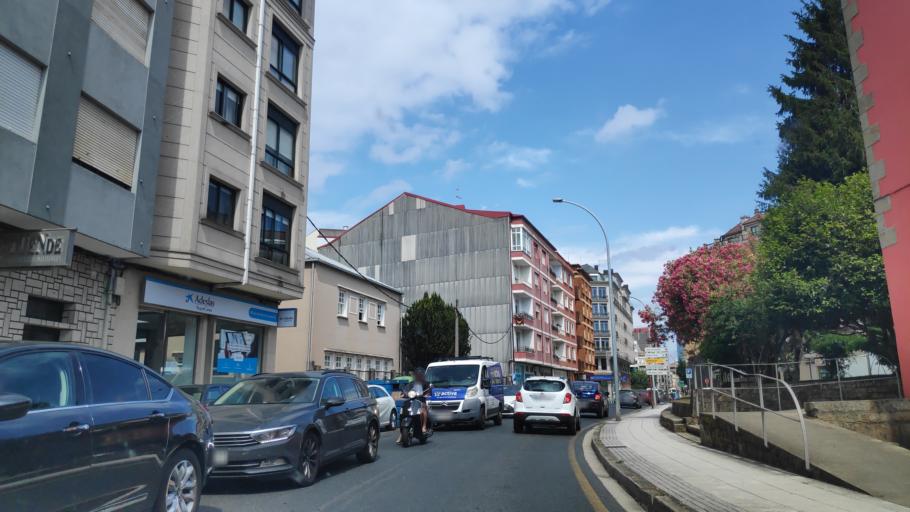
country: ES
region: Galicia
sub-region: Provincia de Pontevedra
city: Vilagarcia de Arousa
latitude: 42.5949
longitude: -8.7629
